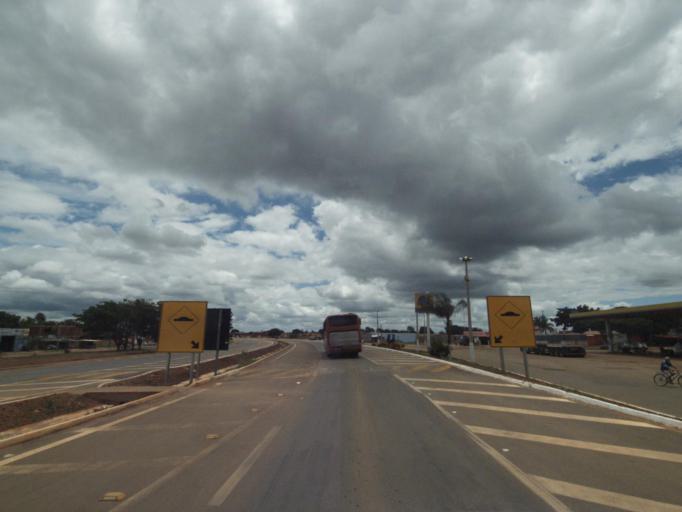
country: BR
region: Federal District
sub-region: Brasilia
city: Brasilia
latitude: -15.7365
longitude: -48.4047
